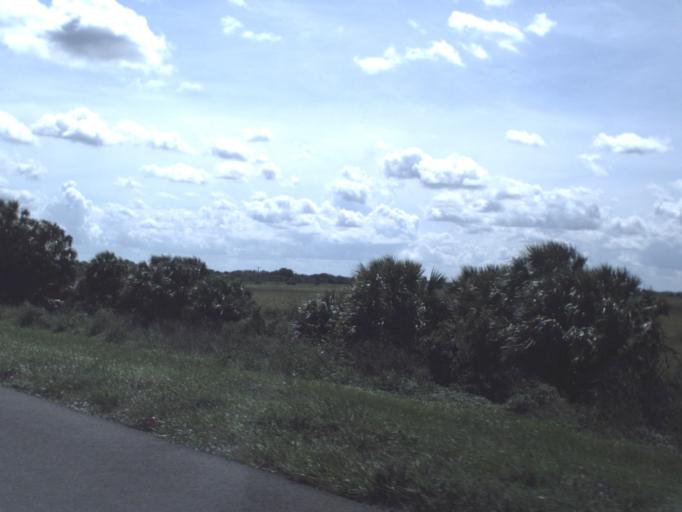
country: US
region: Florida
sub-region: Glades County
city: Moore Haven
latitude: 26.8352
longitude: -81.1917
